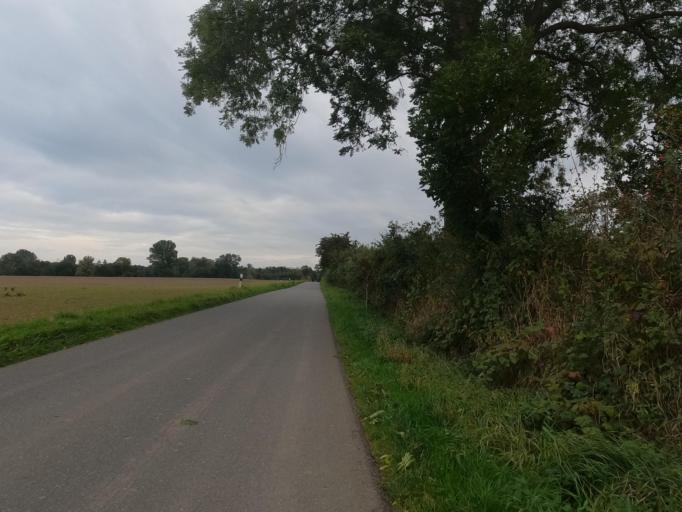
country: DE
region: Schleswig-Holstein
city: Neukirchen
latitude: 54.3068
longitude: 11.0444
